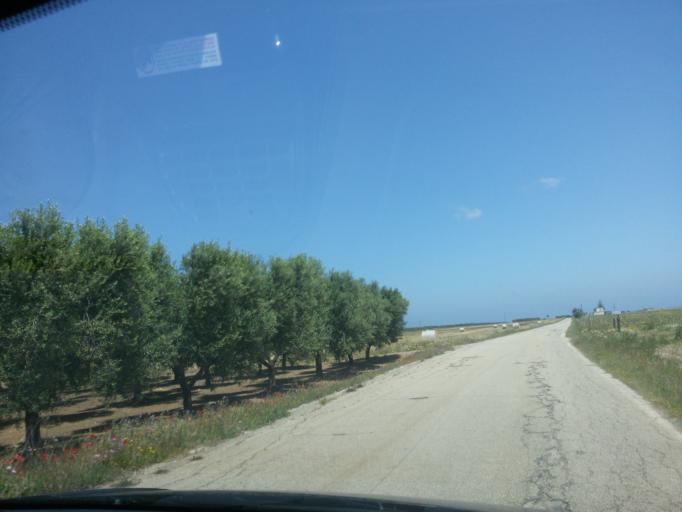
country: IT
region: Apulia
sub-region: Provincia di Brindisi
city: Mesagne
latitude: 40.6513
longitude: 17.8384
